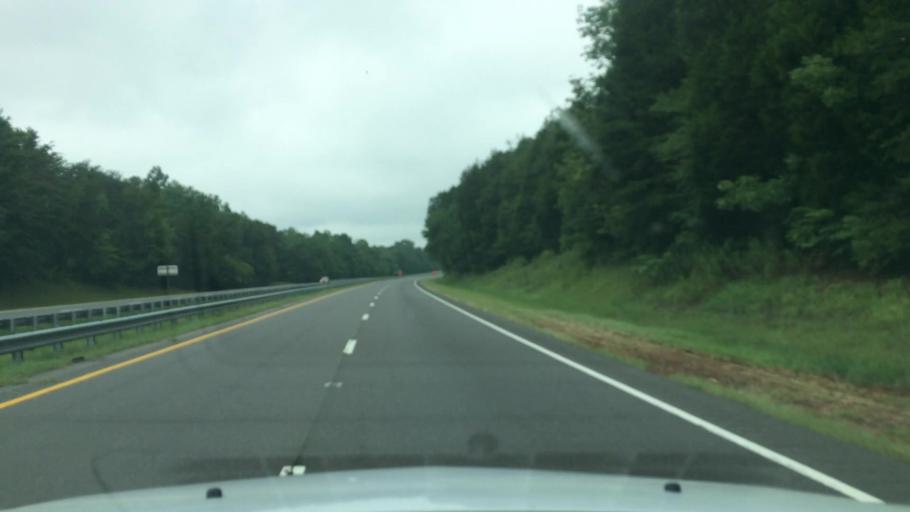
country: US
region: North Carolina
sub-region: Forsyth County
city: Lewisville
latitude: 36.1017
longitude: -80.4977
